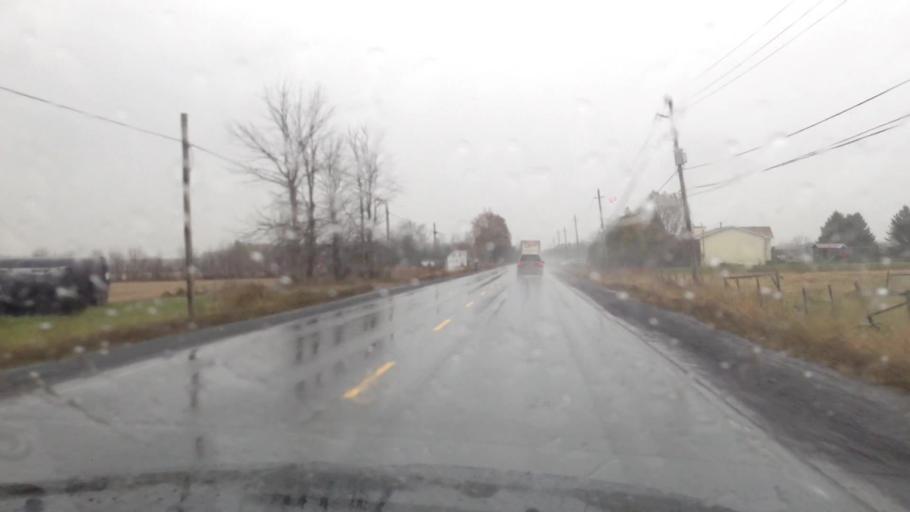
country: CA
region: Ontario
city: Bourget
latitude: 45.2834
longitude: -75.3186
